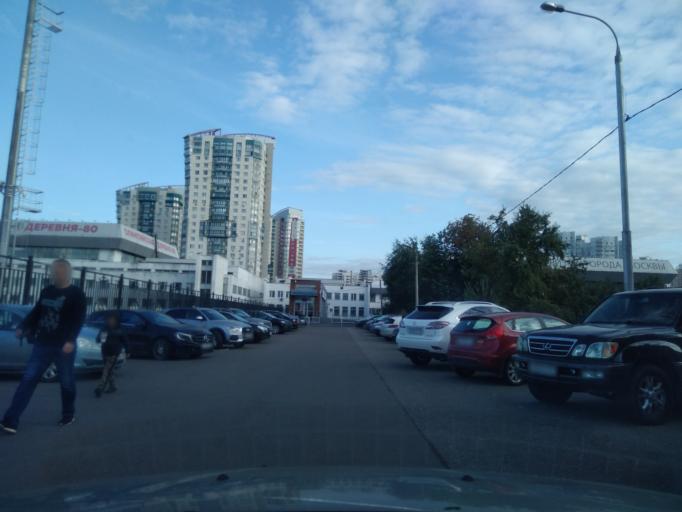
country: RU
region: Moscow
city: Nikulino
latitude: 55.6767
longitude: 37.4722
